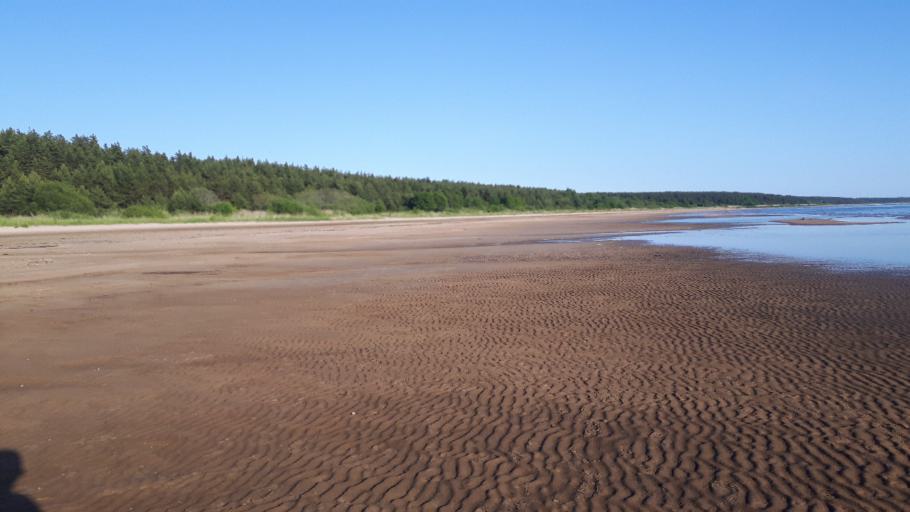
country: LV
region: Salacgrivas
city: Salacgriva
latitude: 57.6931
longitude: 24.3512
